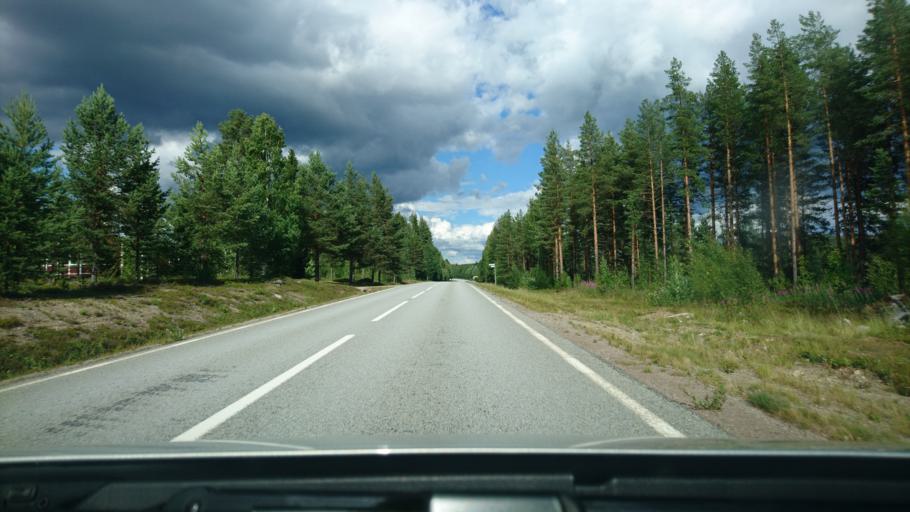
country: SE
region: Vaesterbotten
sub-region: Asele Kommun
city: Asele
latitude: 63.7924
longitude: 17.0881
